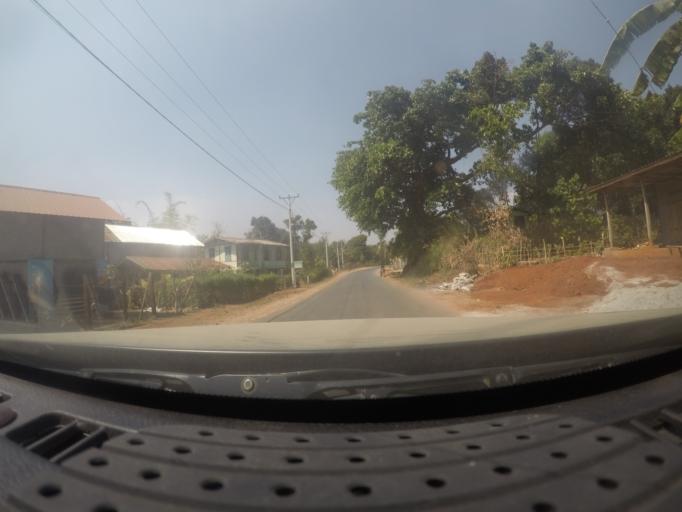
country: MM
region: Shan
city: Taunggyi
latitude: 21.0524
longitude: 96.5121
